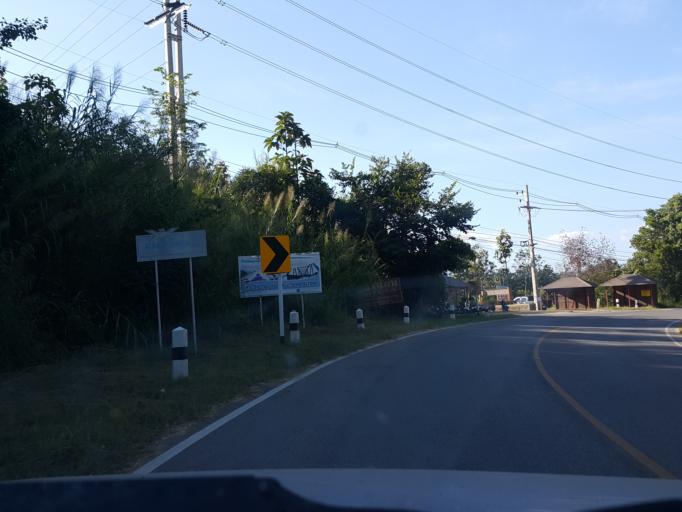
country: TH
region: Mae Hong Son
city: Mae Hi
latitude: 19.3058
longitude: 98.4532
